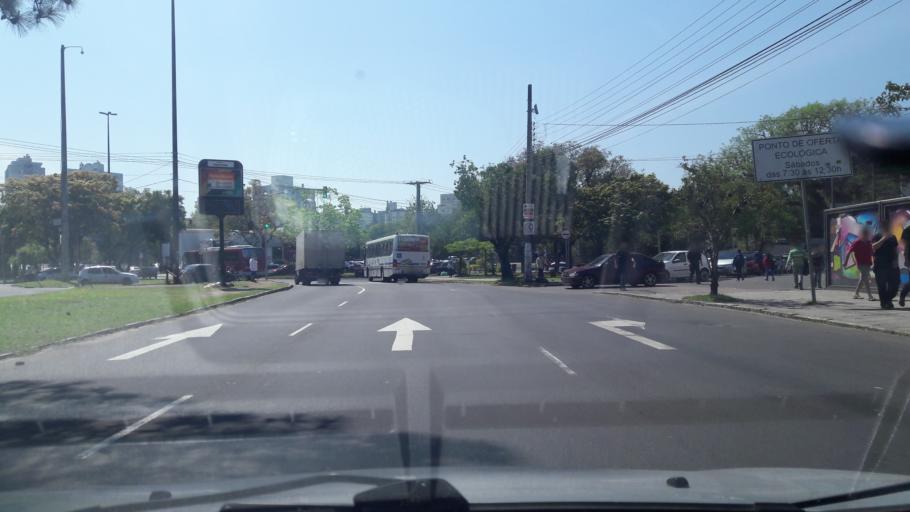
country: BR
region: Rio Grande do Sul
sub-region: Guaiba
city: Guaiba
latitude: -30.1107
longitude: -51.2544
